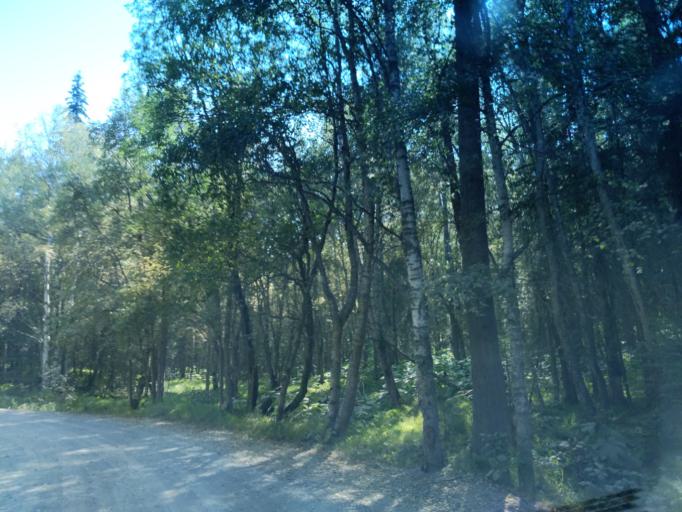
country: US
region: Alaska
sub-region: Anchorage Municipality
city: Anchorage
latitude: 61.1628
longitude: -150.0217
